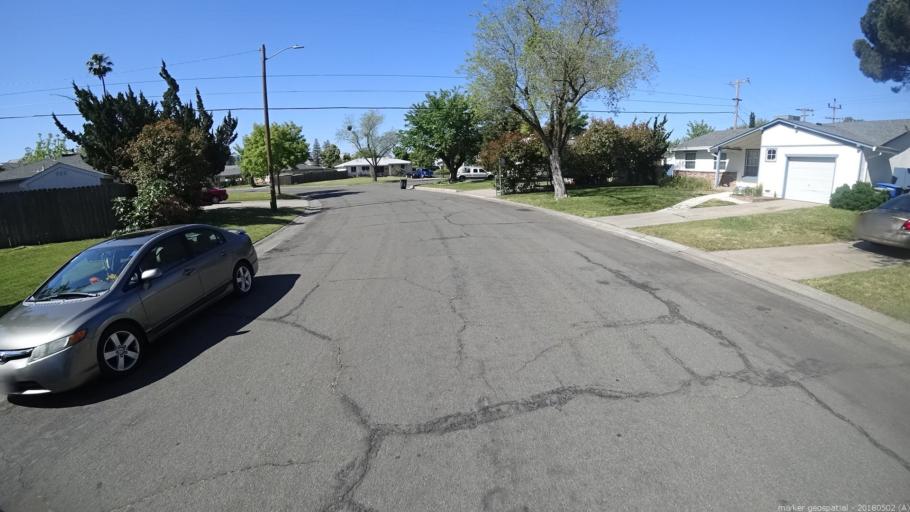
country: US
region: California
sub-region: Sacramento County
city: Arden-Arcade
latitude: 38.6049
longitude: -121.4276
